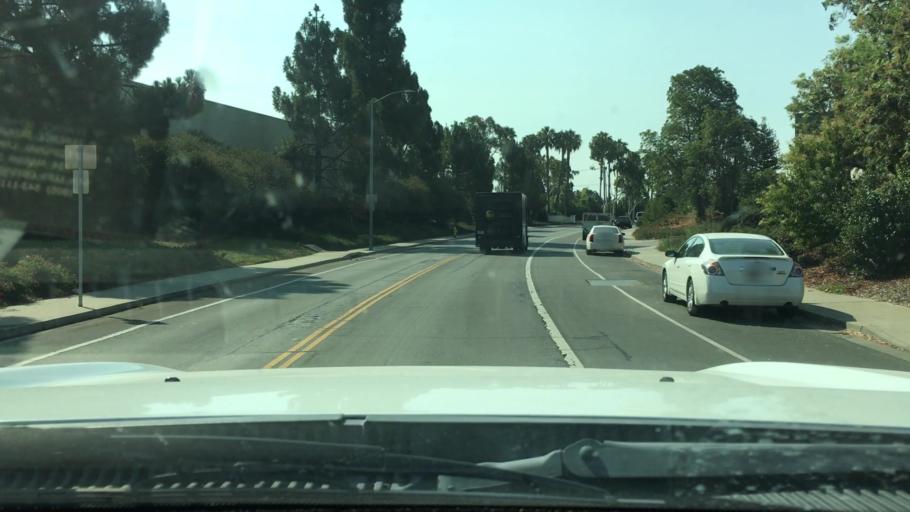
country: US
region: California
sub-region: San Luis Obispo County
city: San Luis Obispo
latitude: 35.2546
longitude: -120.6412
